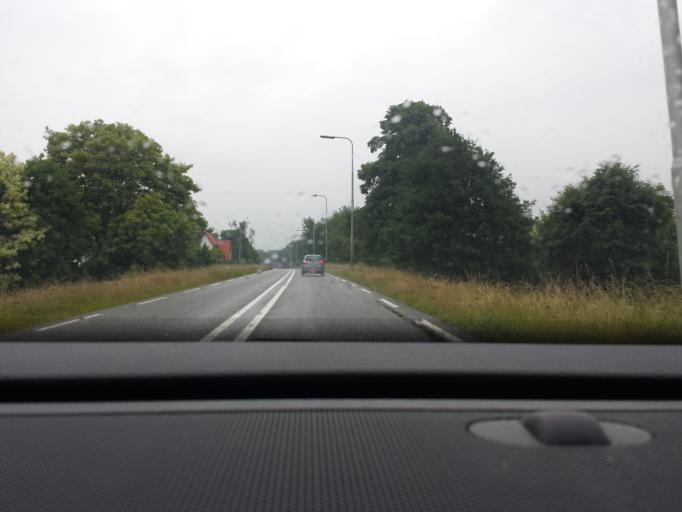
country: NL
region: Overijssel
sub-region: Gemeente Haaksbergen
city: Haaksbergen
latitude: 52.1533
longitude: 6.7494
